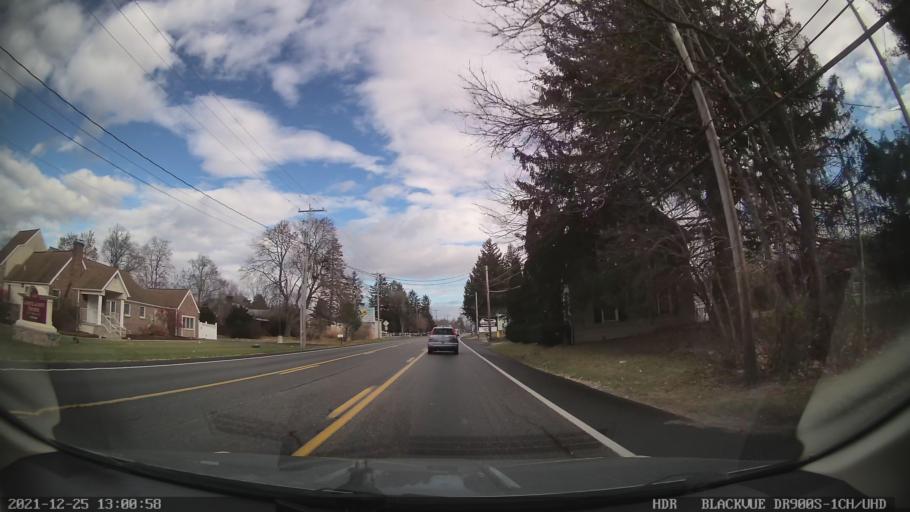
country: US
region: Pennsylvania
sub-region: Adams County
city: Lake Heritage
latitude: 39.8503
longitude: -77.1728
